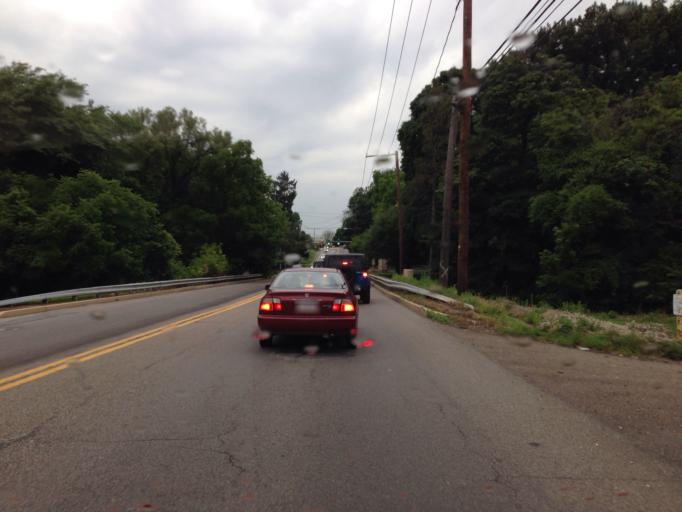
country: US
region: Pennsylvania
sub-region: Lancaster County
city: Lancaster
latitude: 40.0596
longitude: -76.3346
